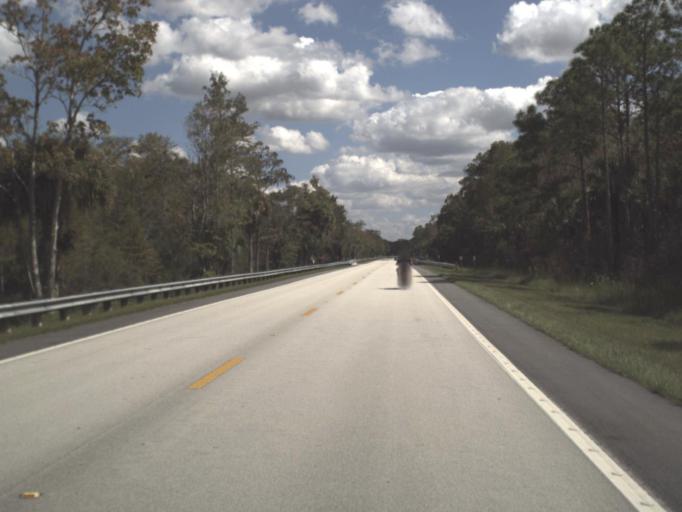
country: US
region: Florida
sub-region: Collier County
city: Marco
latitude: 25.8818
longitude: -81.2489
